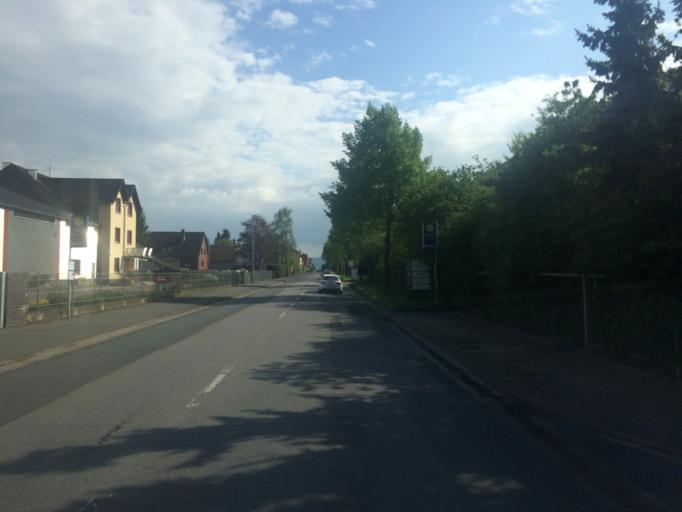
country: DE
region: Lower Saxony
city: Gross Munzel
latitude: 52.3709
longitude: 9.4794
